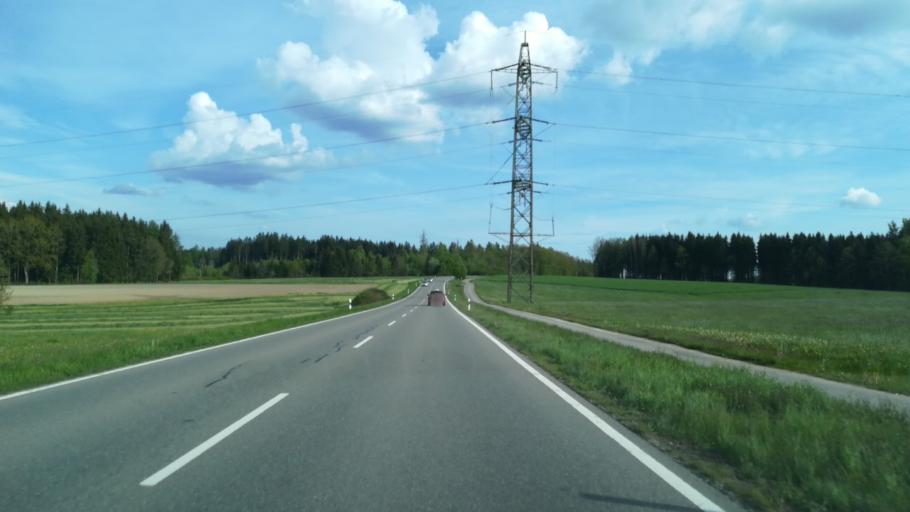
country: DE
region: Baden-Wuerttemberg
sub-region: Freiburg Region
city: Muhlingen
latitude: 47.9395
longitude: 9.0459
